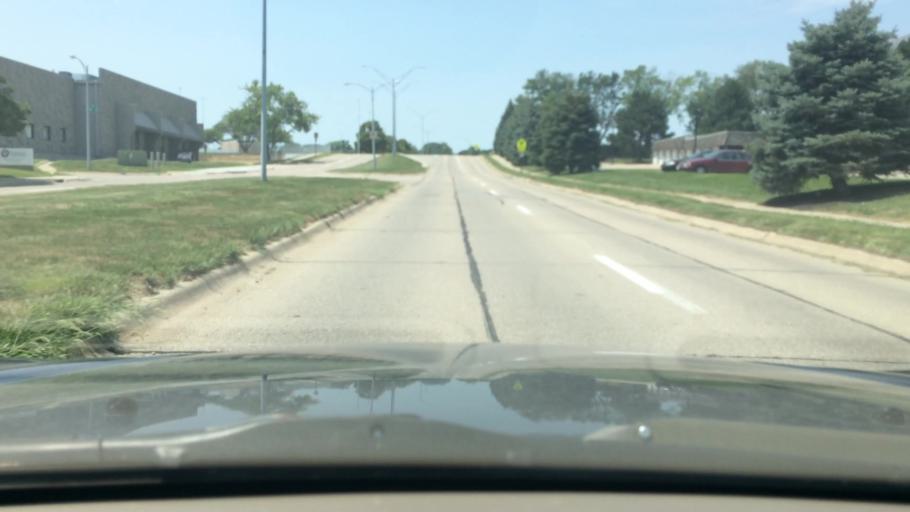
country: US
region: Nebraska
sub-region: Douglas County
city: Ralston
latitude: 41.2015
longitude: -96.0459
